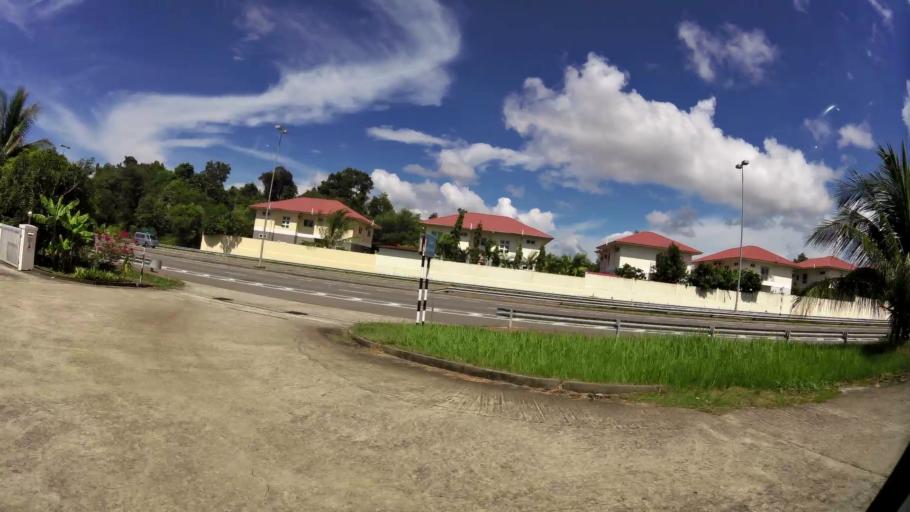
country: BN
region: Brunei and Muara
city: Bandar Seri Begawan
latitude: 4.9729
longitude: 114.9540
